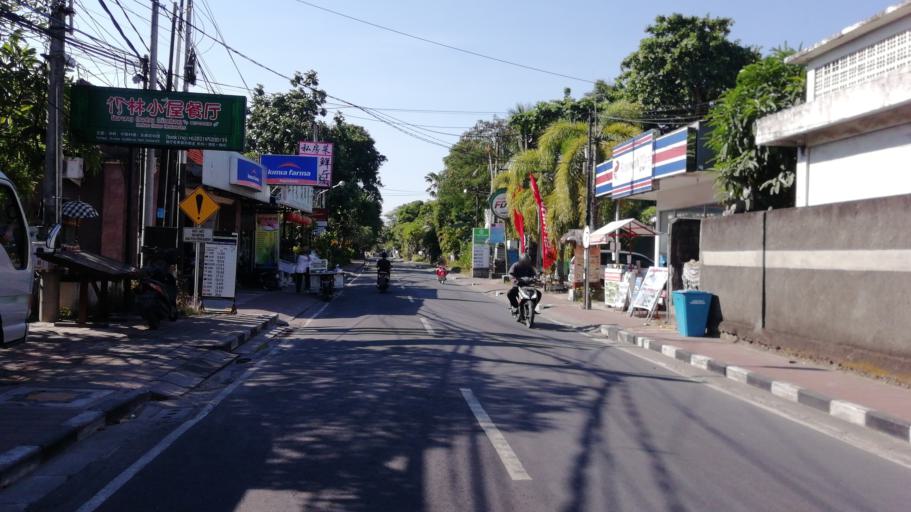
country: ID
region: Bali
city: Bualu
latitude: -8.7652
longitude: 115.2220
